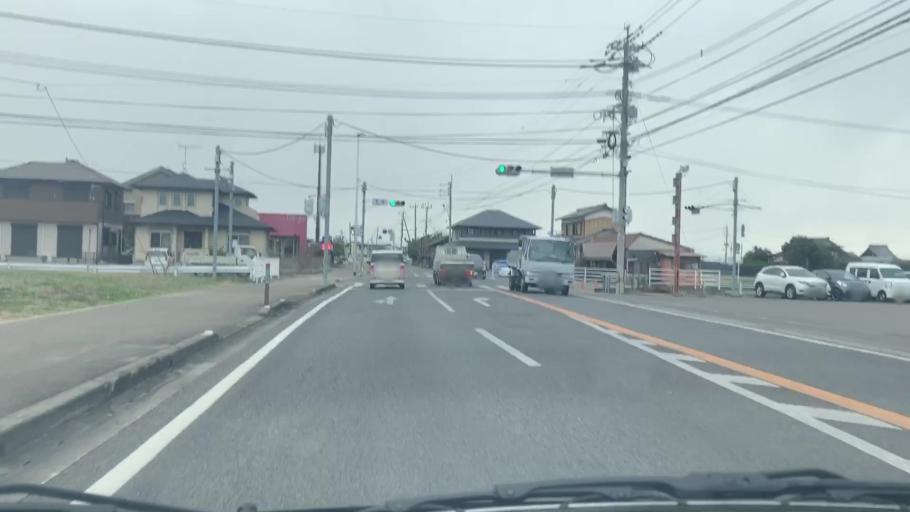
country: JP
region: Saga Prefecture
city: Saga-shi
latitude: 33.1850
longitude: 130.1921
